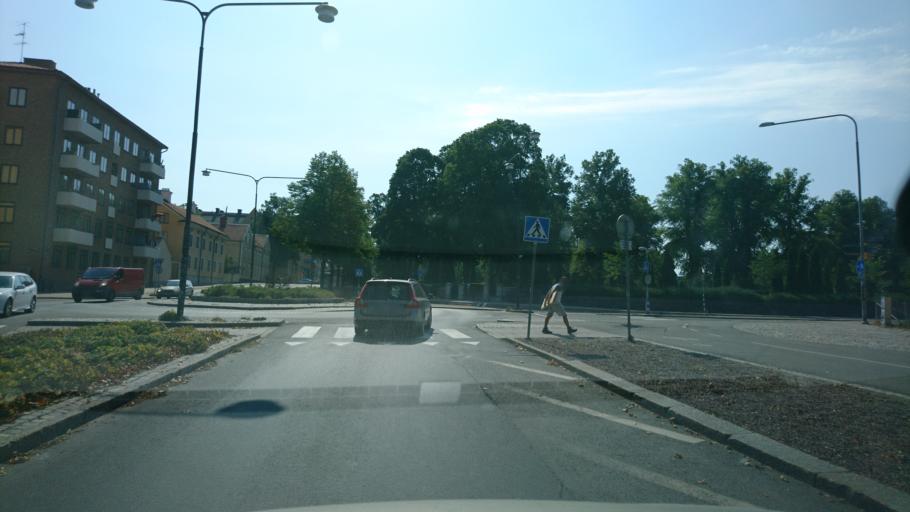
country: SE
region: Uppsala
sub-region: Uppsala Kommun
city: Uppsala
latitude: 59.8579
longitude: 17.6247
